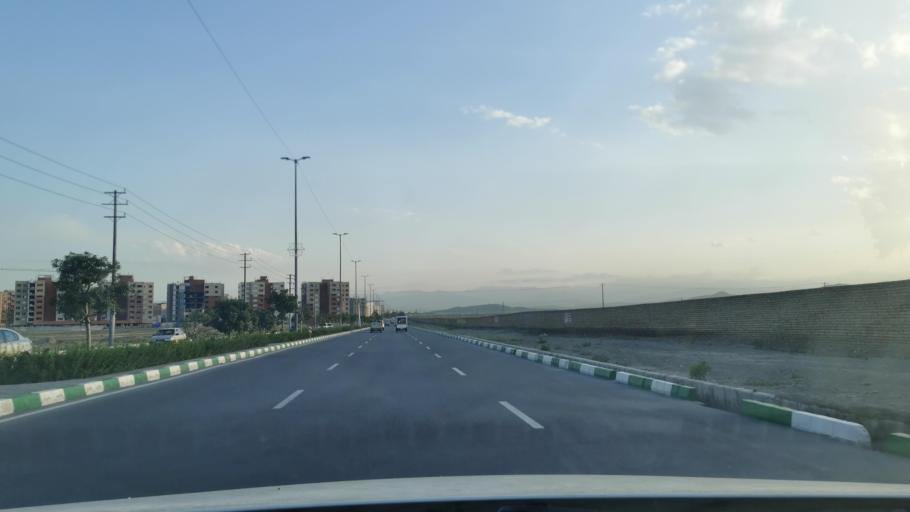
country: IR
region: Razavi Khorasan
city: Mashhad
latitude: 36.3974
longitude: 59.4758
